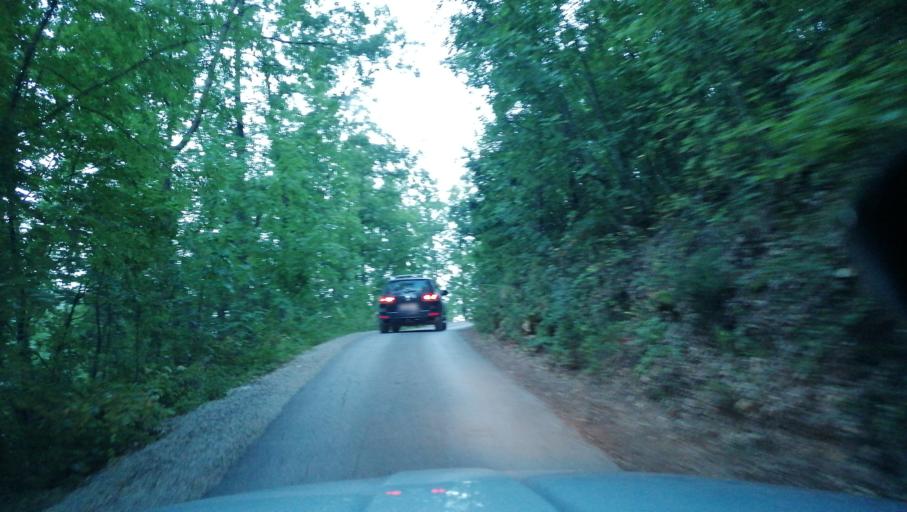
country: RS
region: Central Serbia
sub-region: Kolubarski Okrug
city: Valjevo
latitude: 44.2335
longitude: 19.8589
